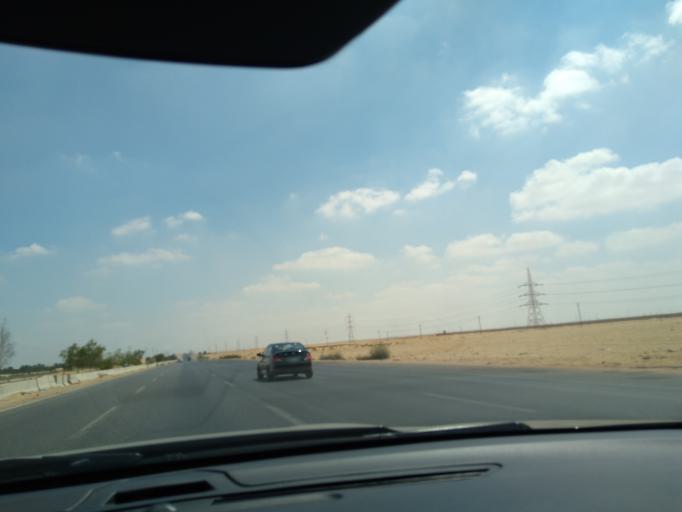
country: EG
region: Al Isma'iliyah
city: At Tall al Kabir
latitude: 30.3611
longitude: 31.9060
